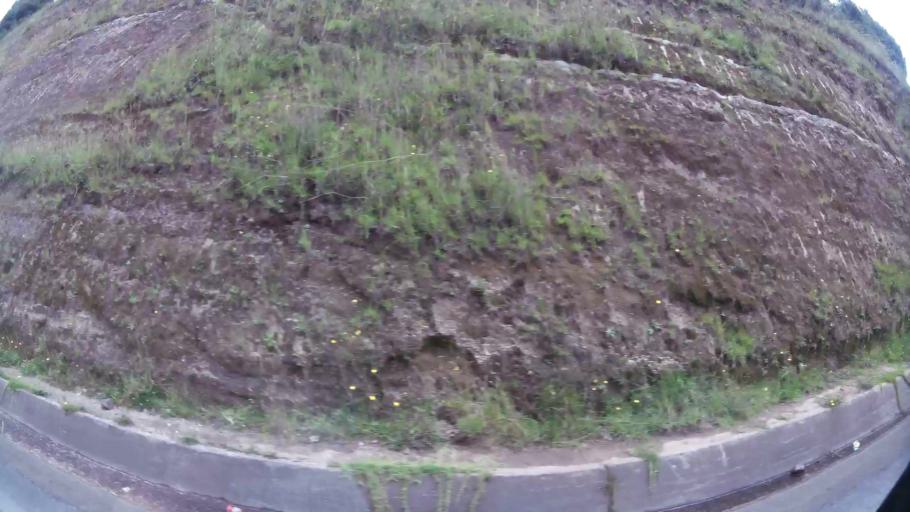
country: EC
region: Pichincha
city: Sangolqui
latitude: -0.3274
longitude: -78.5191
